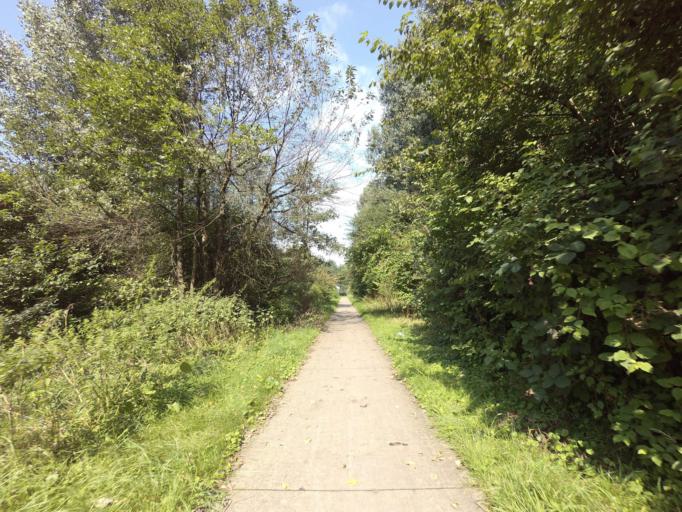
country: NL
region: Flevoland
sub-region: Gemeente Lelystad
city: Lelystad
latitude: 52.5283
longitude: 5.5190
